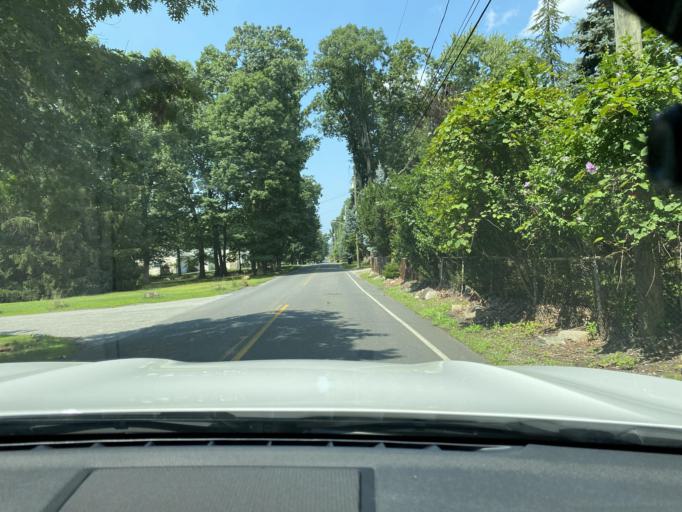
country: US
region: New York
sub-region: Rockland County
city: Airmont
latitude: 41.0921
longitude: -74.1123
